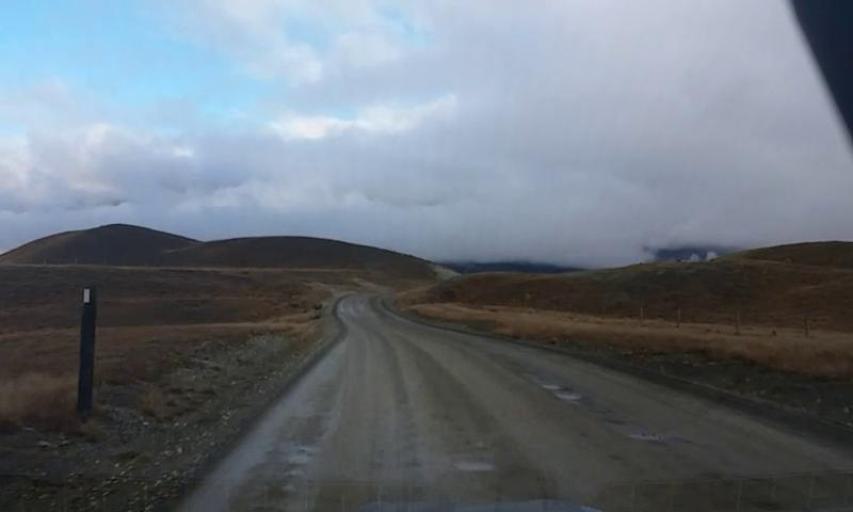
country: NZ
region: Canterbury
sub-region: Ashburton District
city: Methven
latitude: -43.6151
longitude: 171.1364
